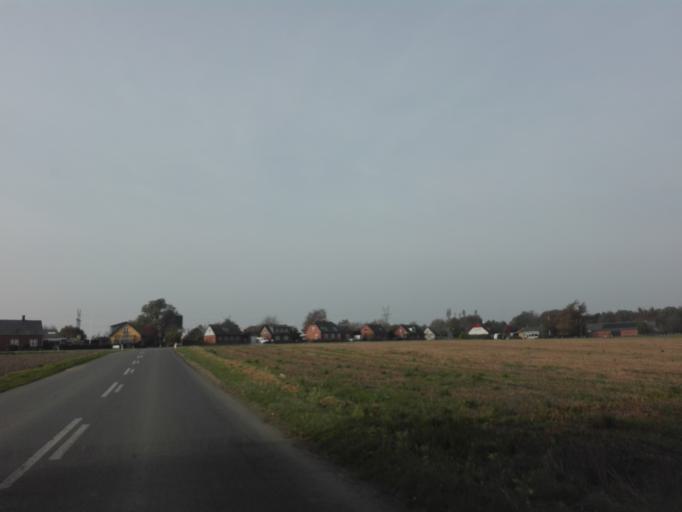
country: DK
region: Central Jutland
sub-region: Odder Kommune
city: Odder
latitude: 55.9958
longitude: 10.1171
